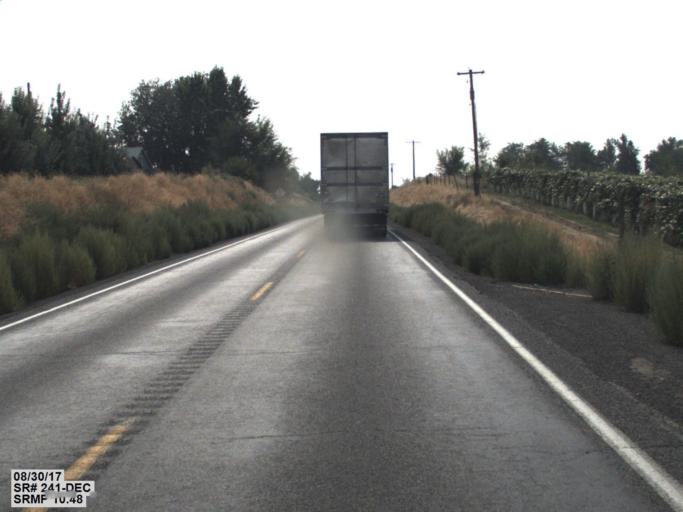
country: US
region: Washington
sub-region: Yakima County
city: Sunnyside
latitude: 46.3485
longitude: -119.9791
